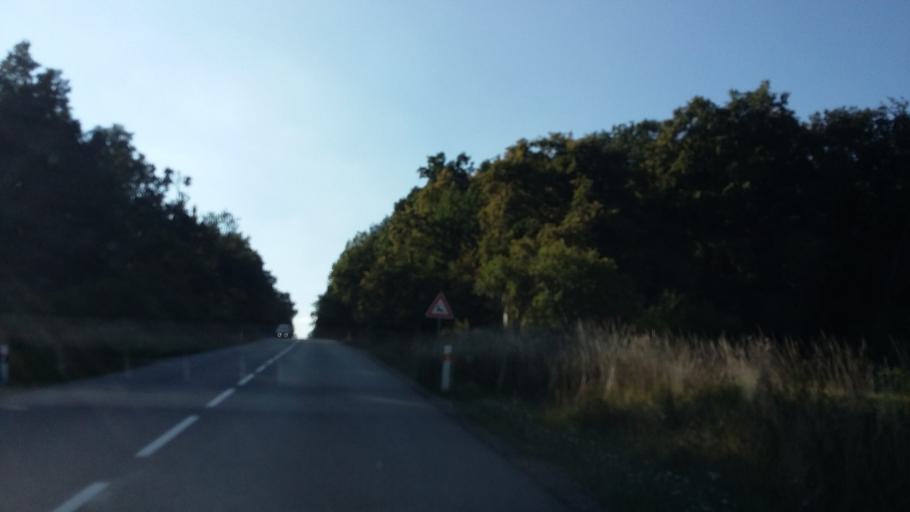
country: CZ
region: South Moravian
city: Ricany
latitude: 49.2195
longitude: 16.3746
